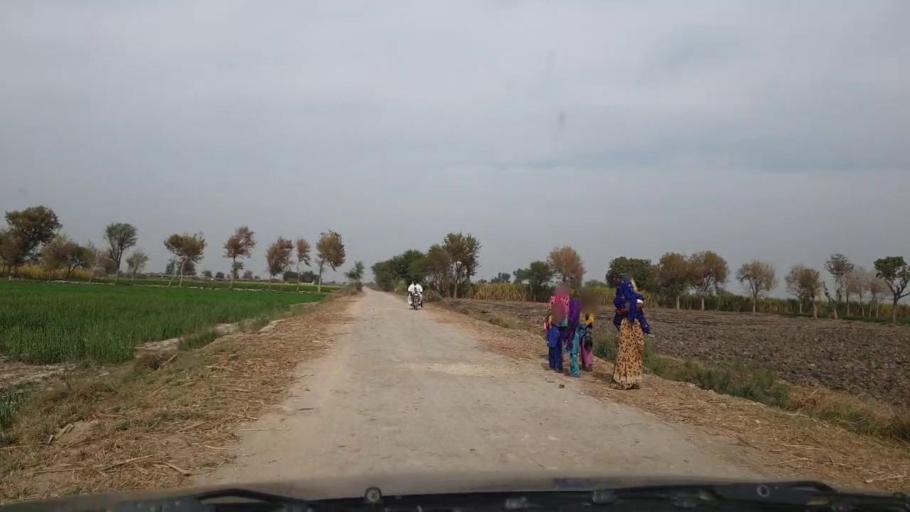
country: PK
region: Sindh
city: Sinjhoro
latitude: 26.0887
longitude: 68.8279
